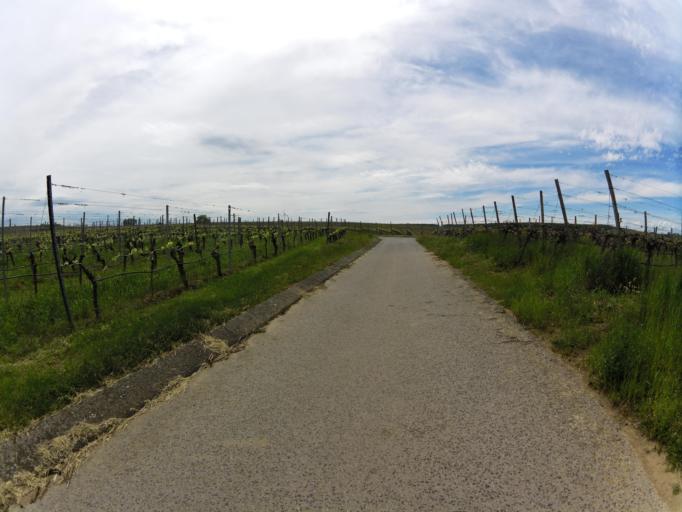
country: DE
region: Bavaria
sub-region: Regierungsbezirk Unterfranken
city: Nordheim
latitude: 49.8549
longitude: 10.1952
